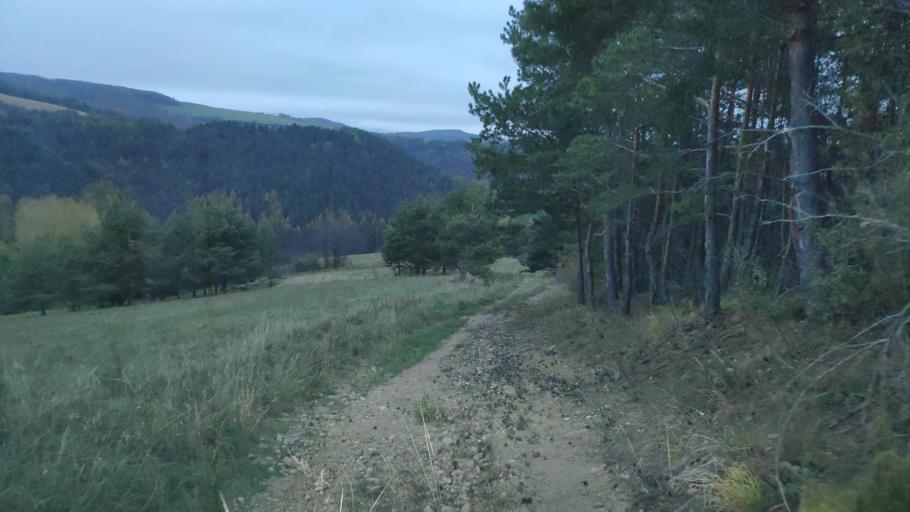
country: SK
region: Presovsky
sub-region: Okres Presov
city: Presov
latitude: 48.9385
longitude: 21.0866
